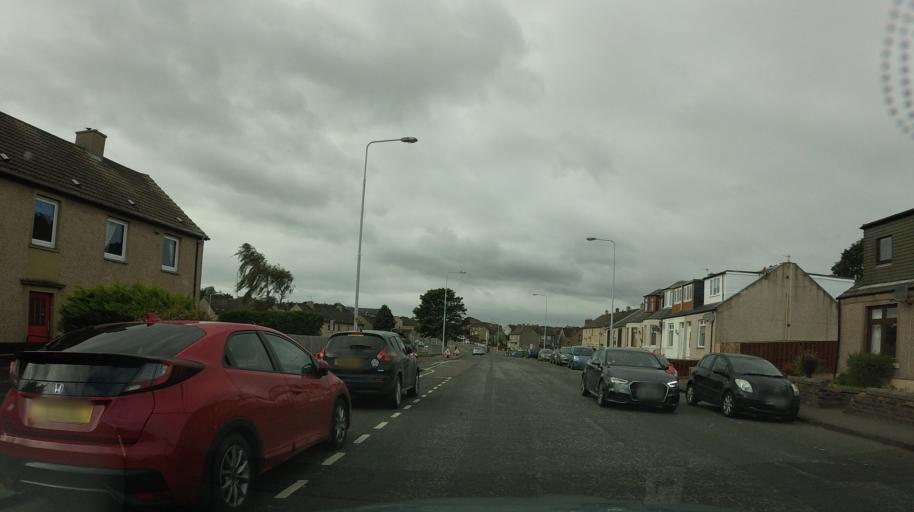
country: GB
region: Scotland
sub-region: Fife
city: Cowdenbeath
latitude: 56.1027
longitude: -3.3531
